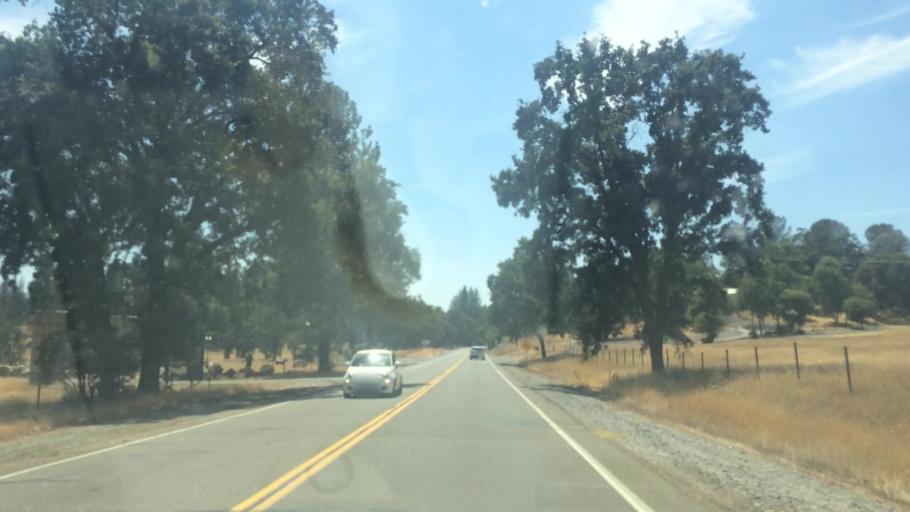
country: US
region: California
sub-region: Amador County
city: Pine Grove
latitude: 38.4041
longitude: -120.7192
